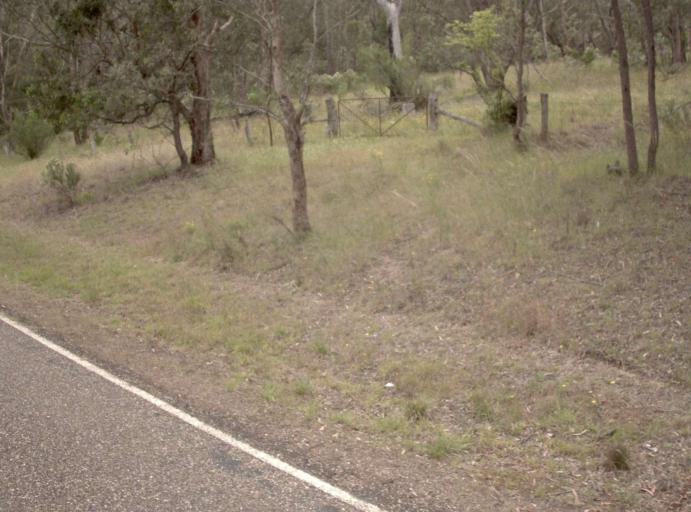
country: AU
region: Victoria
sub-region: East Gippsland
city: Bairnsdale
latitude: -37.5356
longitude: 147.2125
